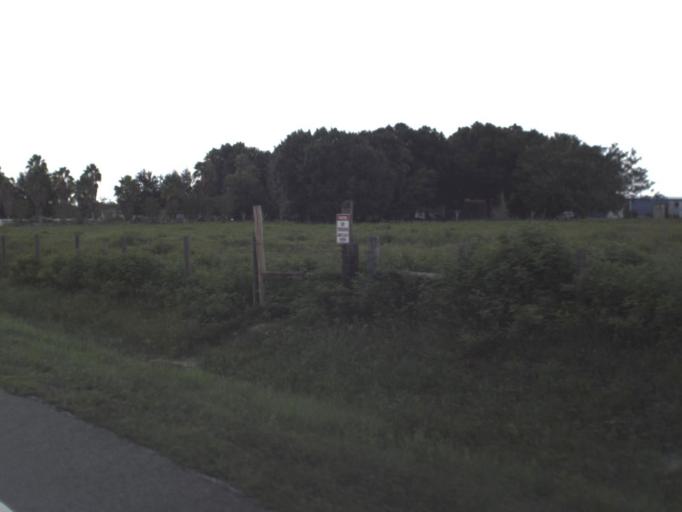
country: US
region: Florida
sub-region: Hillsborough County
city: Wimauma
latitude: 27.4600
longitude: -82.1138
